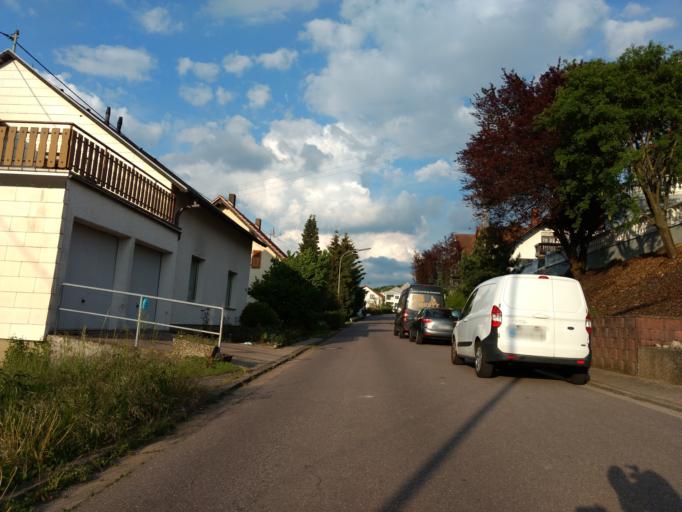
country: DE
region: Saarland
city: Beckingen
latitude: 49.4071
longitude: 6.6649
